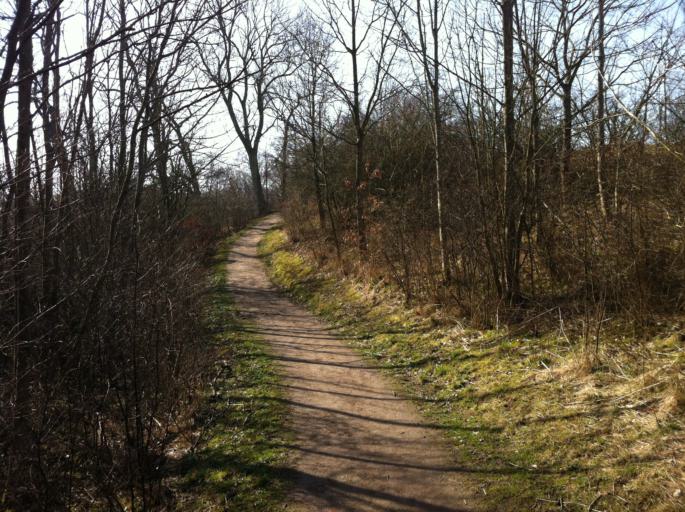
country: SE
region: Skane
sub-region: Helsingborg
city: Gantofta
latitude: 56.0002
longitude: 12.7833
